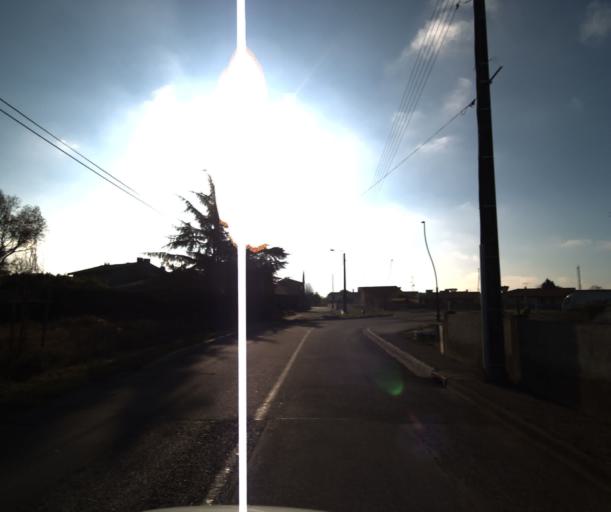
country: FR
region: Midi-Pyrenees
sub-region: Departement de la Haute-Garonne
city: Colomiers
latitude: 43.5967
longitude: 1.3589
